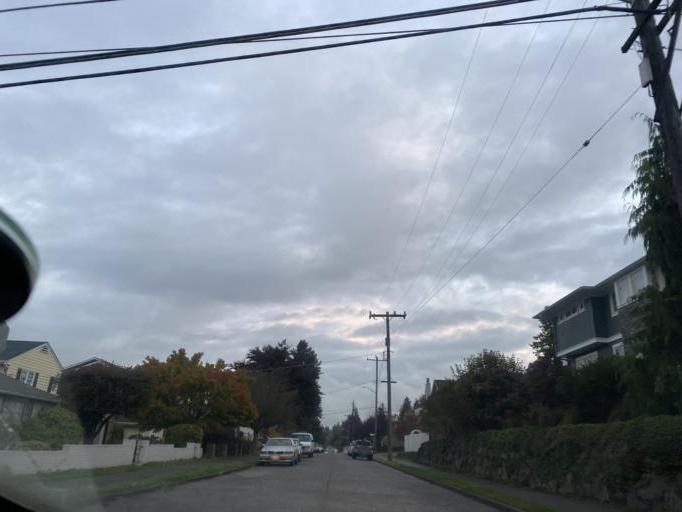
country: US
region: Washington
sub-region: King County
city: Seattle
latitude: 47.6359
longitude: -122.3957
